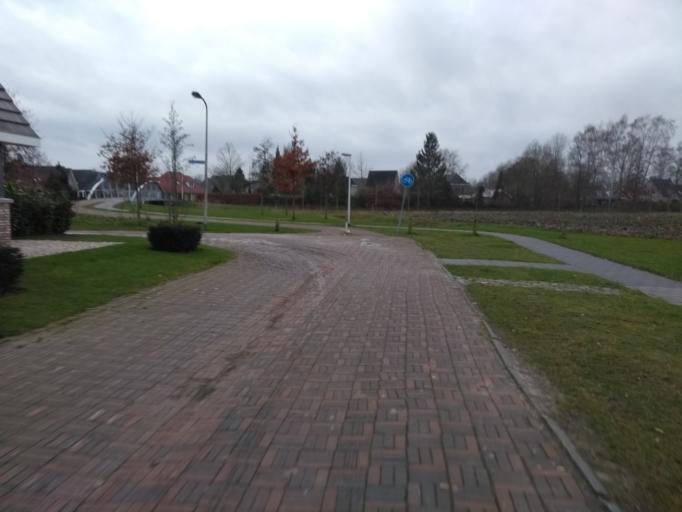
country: NL
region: Overijssel
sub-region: Gemeente Almelo
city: Almelo
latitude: 52.3730
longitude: 6.6990
